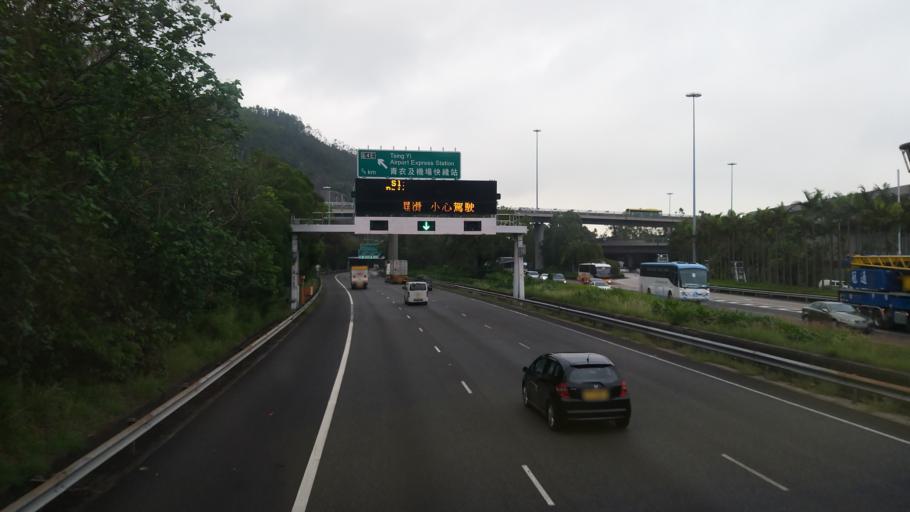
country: HK
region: Tsuen Wan
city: Tsuen Wan
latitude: 22.3558
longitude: 114.0843
